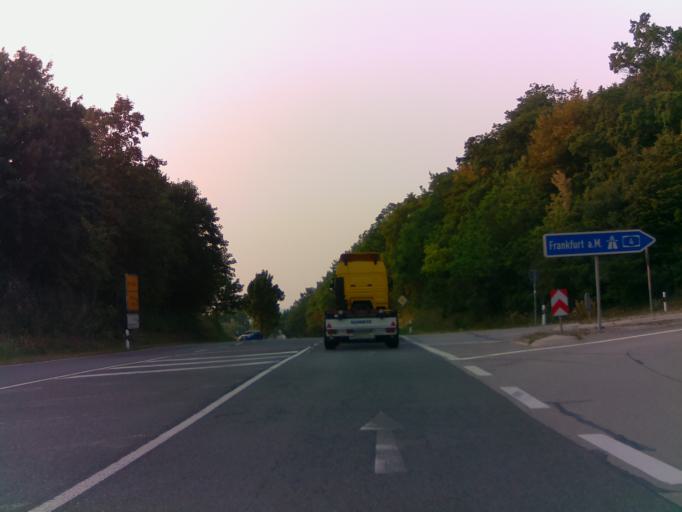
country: DE
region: Thuringia
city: Troistedt
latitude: 50.9500
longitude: 11.2418
